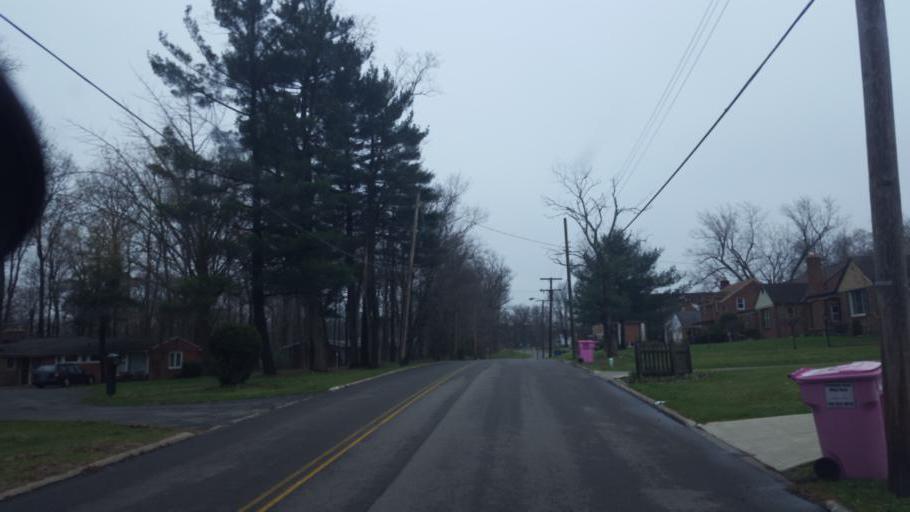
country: US
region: Ohio
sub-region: Richland County
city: Mansfield
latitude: 40.7561
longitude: -82.5478
